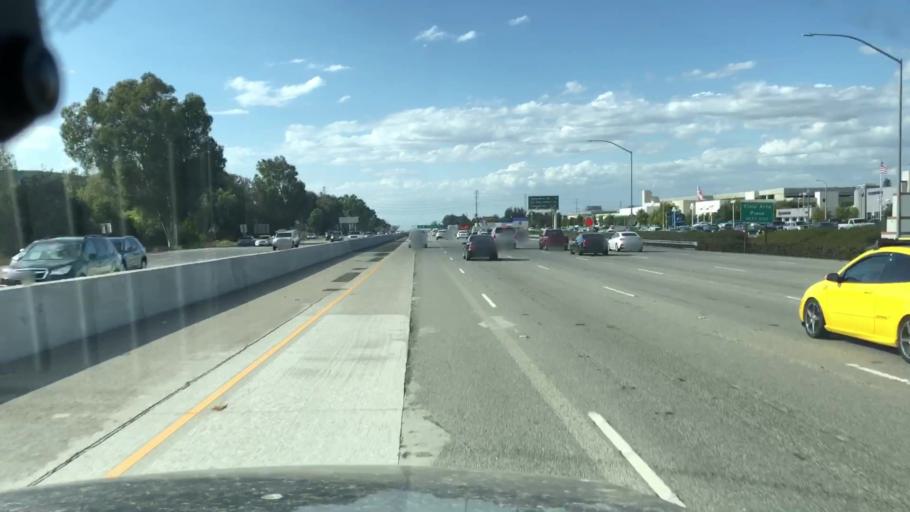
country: US
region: California
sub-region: Ventura County
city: Thousand Oaks
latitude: 34.1604
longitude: -118.8292
